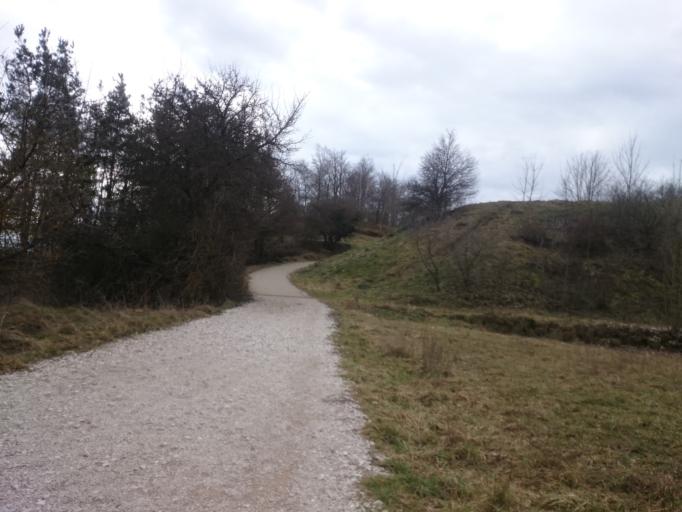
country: DE
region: Bavaria
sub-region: Upper Palatinate
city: Kallmunz
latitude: 49.1646
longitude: 11.9524
